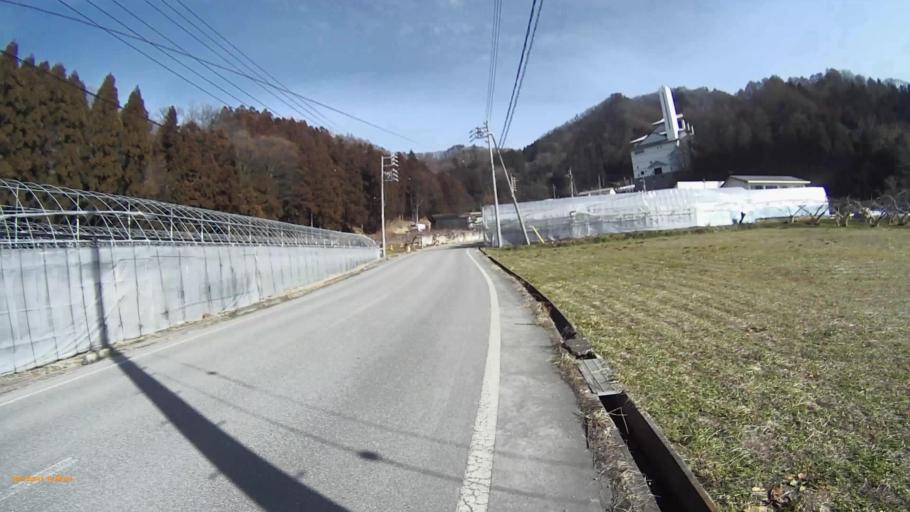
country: JP
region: Nagano
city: Nakano
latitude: 36.7472
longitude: 138.3807
